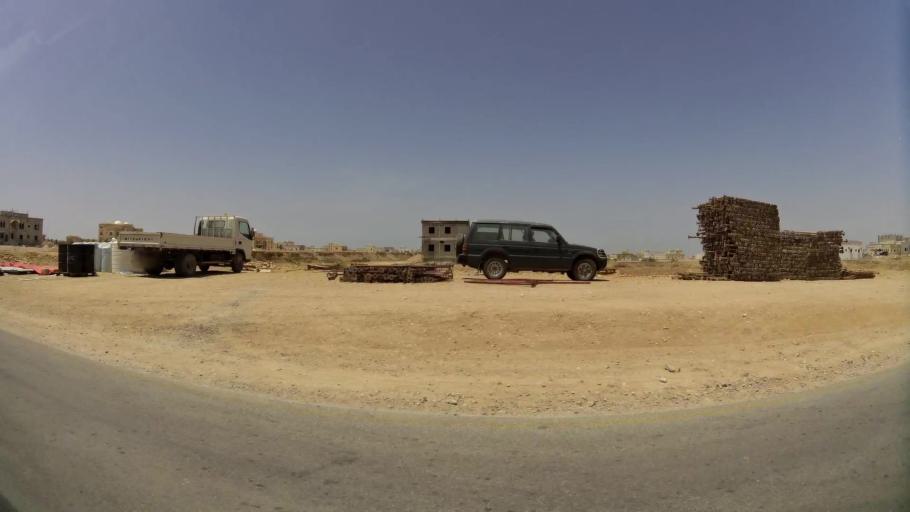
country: OM
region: Zufar
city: Salalah
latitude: 17.0822
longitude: 54.1919
